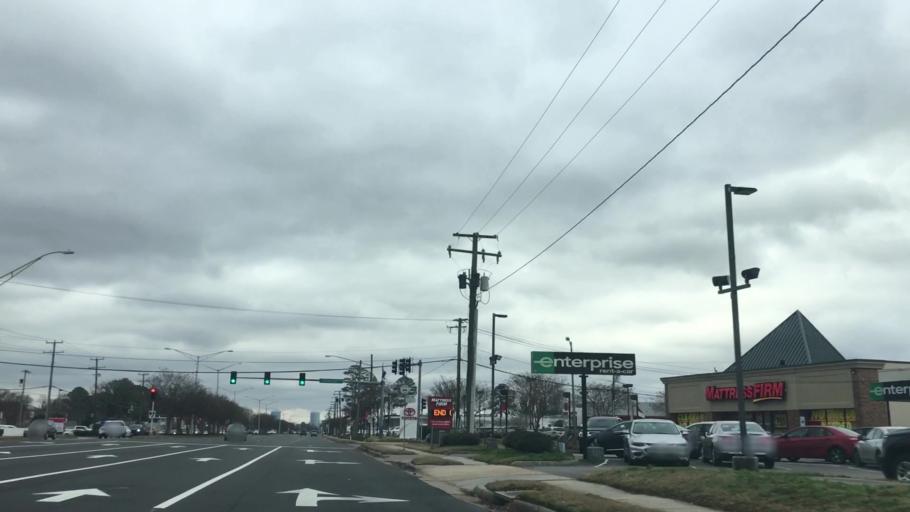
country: US
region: Virginia
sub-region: City of Chesapeake
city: Chesapeake
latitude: 36.8490
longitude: -76.1651
